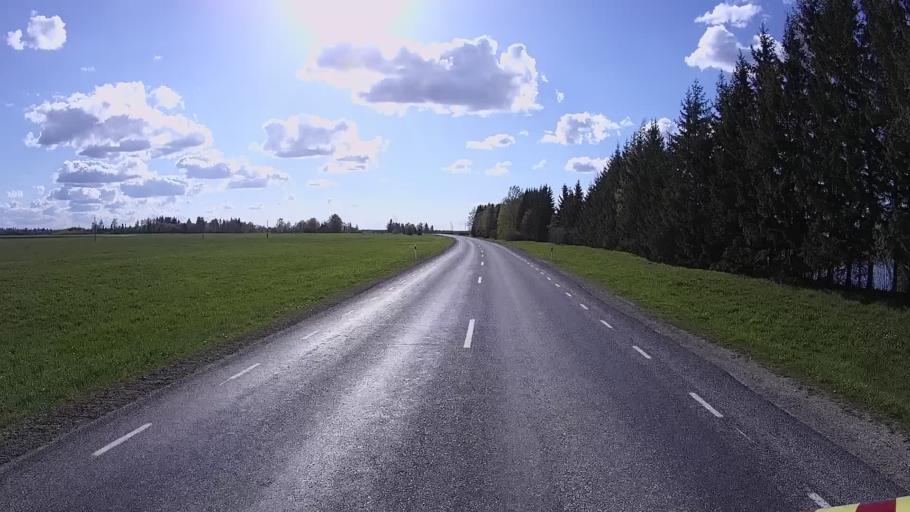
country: EE
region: Jogevamaa
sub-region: Jogeva linn
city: Jogeva
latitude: 58.7398
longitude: 26.2515
